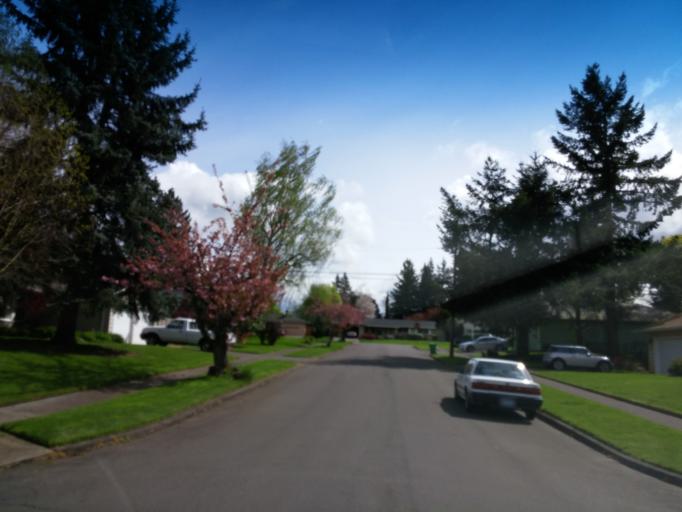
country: US
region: Oregon
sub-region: Washington County
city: Cedar Hills
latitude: 45.5090
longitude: -122.8023
